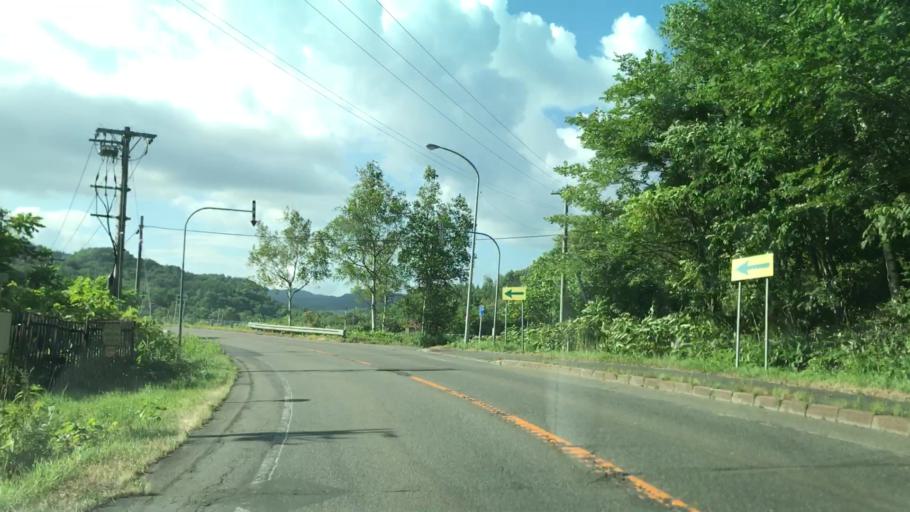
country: JP
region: Hokkaido
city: Shimo-furano
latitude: 42.8960
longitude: 142.4300
